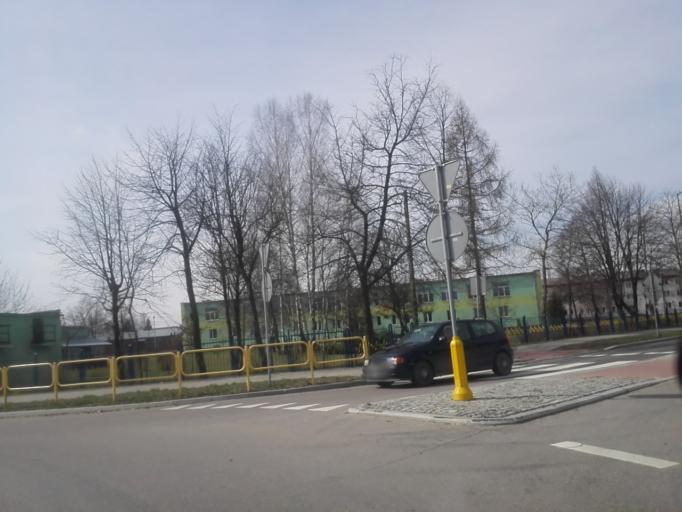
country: PL
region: Podlasie
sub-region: Powiat sejnenski
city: Sejny
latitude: 54.1082
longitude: 23.3407
